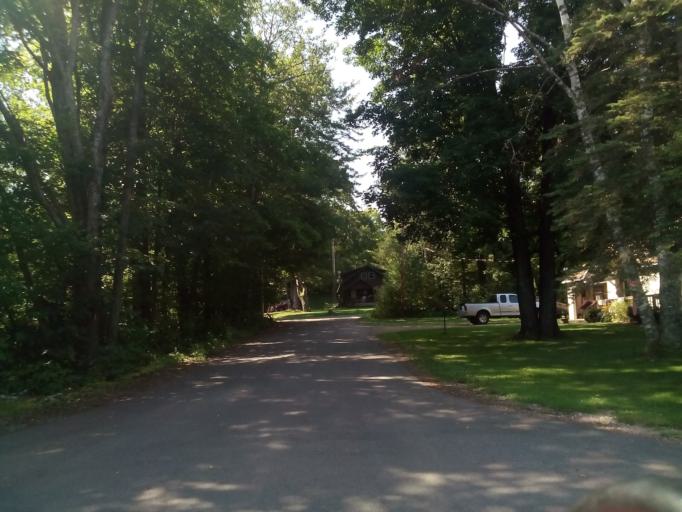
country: US
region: Wisconsin
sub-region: Menominee County
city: Legend Lake
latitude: 45.2994
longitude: -88.5223
